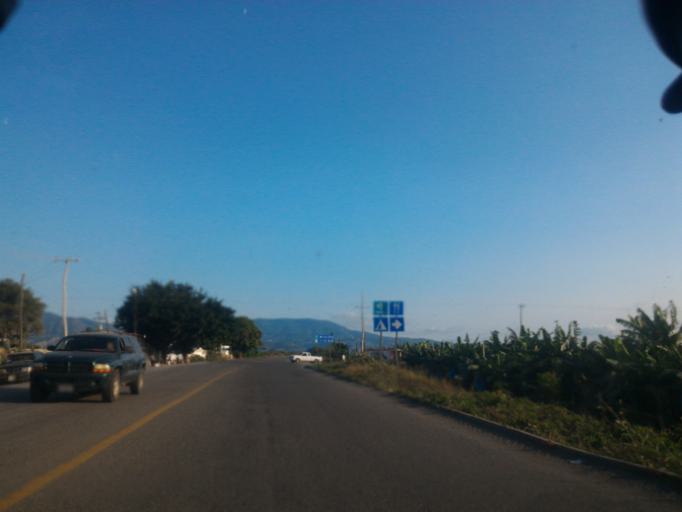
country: MX
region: Michoacan
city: Coahuayana Viejo
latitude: 18.7101
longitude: -103.7101
